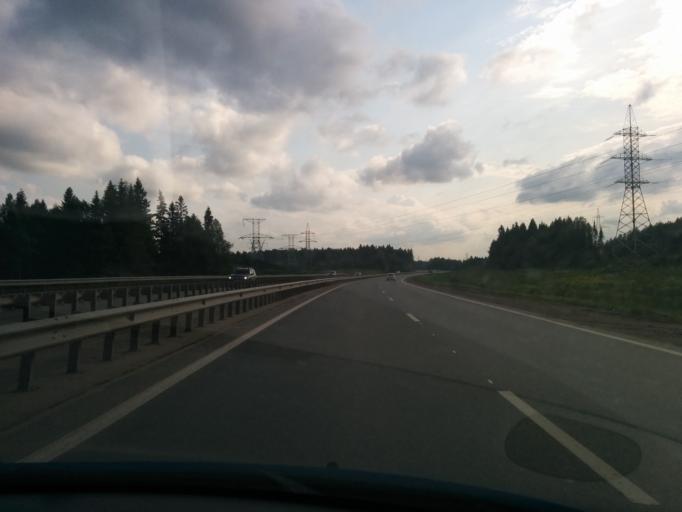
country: RU
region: Perm
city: Ferma
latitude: 58.0175
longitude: 56.4135
